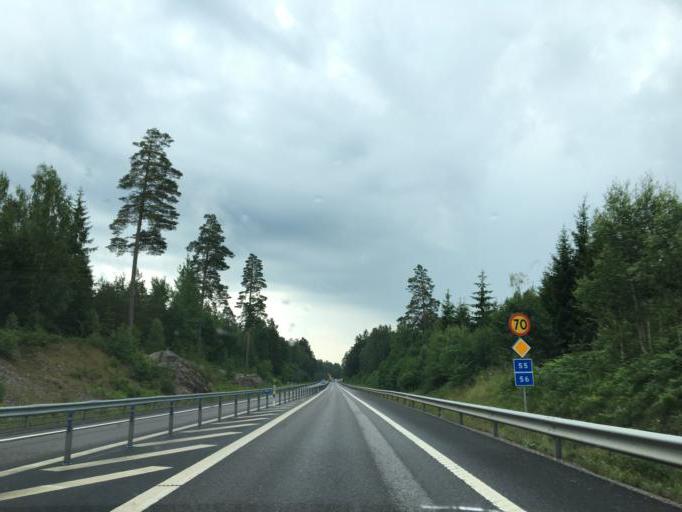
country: SE
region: OEstergoetland
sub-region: Norrkopings Kommun
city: Jursla
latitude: 58.7953
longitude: 16.1552
